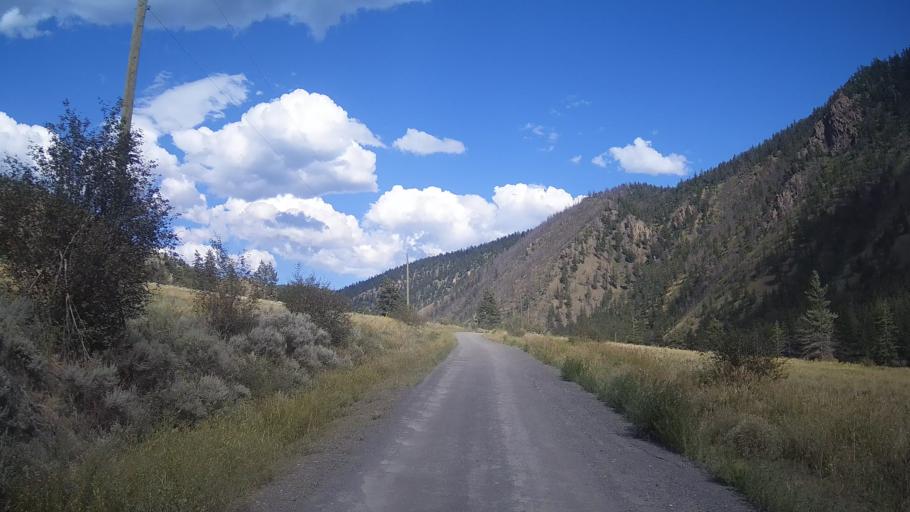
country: CA
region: British Columbia
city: Lillooet
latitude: 51.2213
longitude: -122.0855
